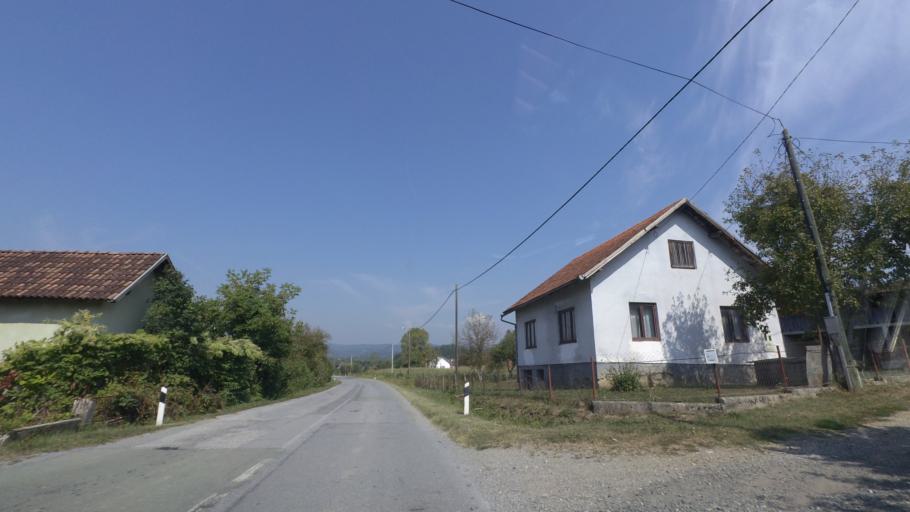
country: HR
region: Sisacko-Moslavacka
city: Dvor
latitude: 45.1070
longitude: 16.2859
